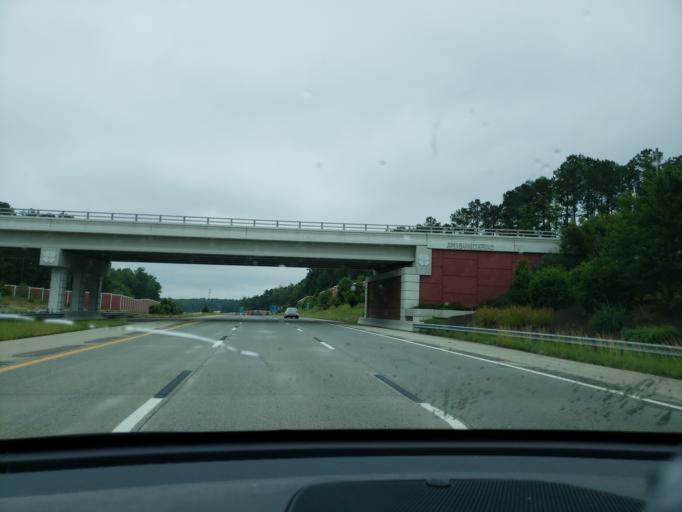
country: US
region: North Carolina
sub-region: Wake County
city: Apex
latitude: 35.7220
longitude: -78.8862
